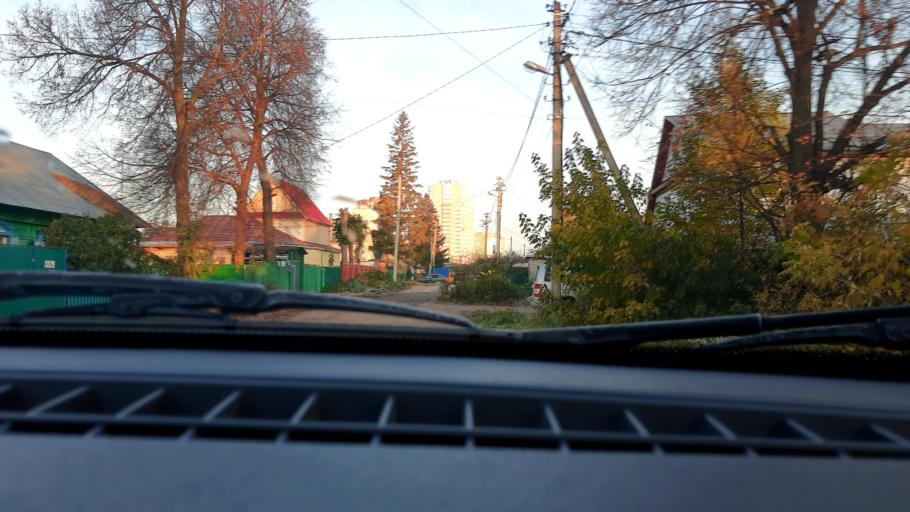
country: RU
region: Bashkortostan
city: Mikhaylovka
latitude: 54.7862
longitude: 55.8773
